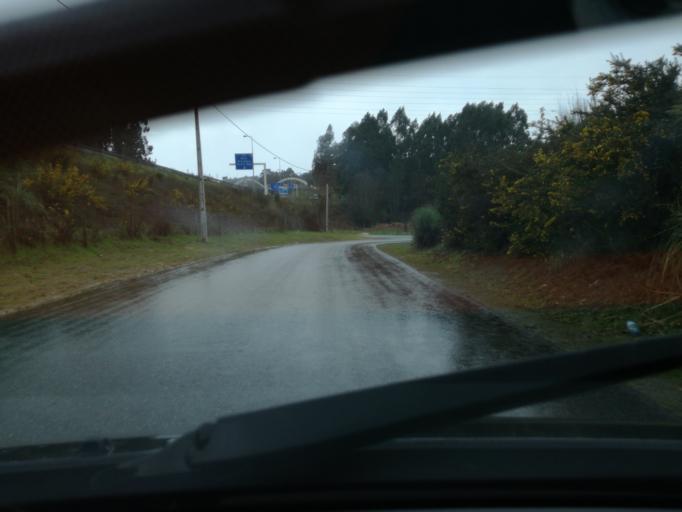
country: PT
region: Porto
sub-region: Valongo
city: Ermesinde
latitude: 41.2408
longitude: -8.5565
